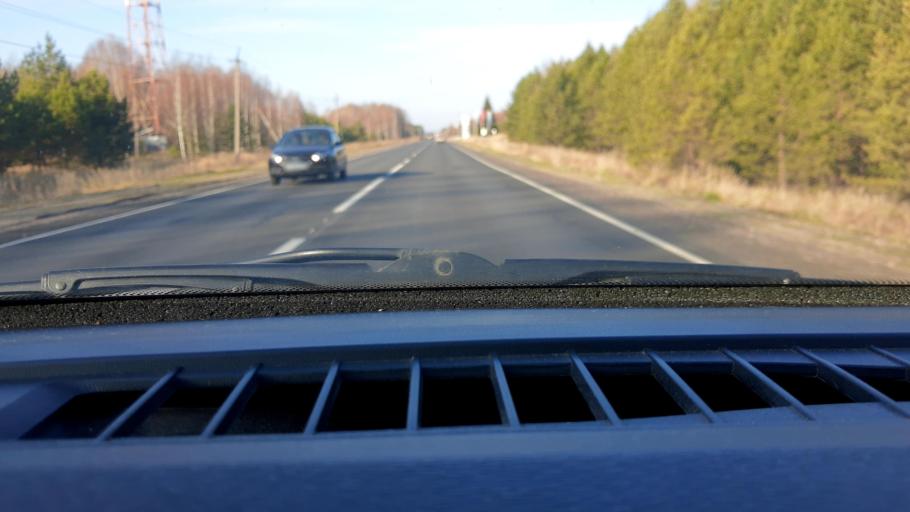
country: RU
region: Nizjnij Novgorod
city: Novaya Balakhna
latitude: 56.5993
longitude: 43.6373
